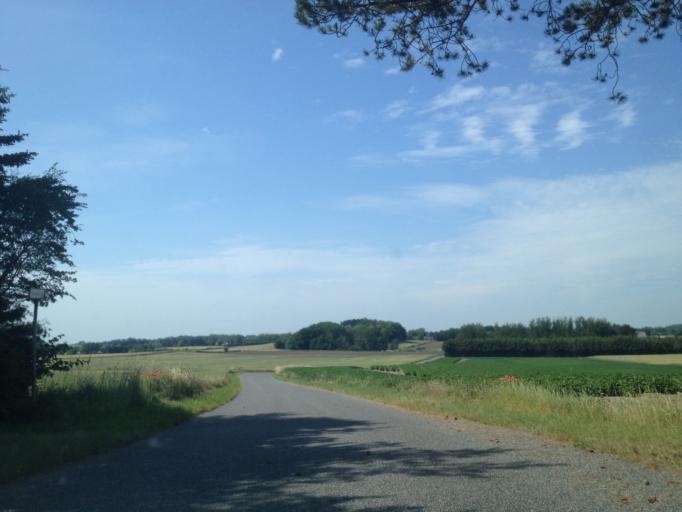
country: DK
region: Central Jutland
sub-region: Samso Kommune
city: Tranebjerg
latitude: 55.8022
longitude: 10.5575
